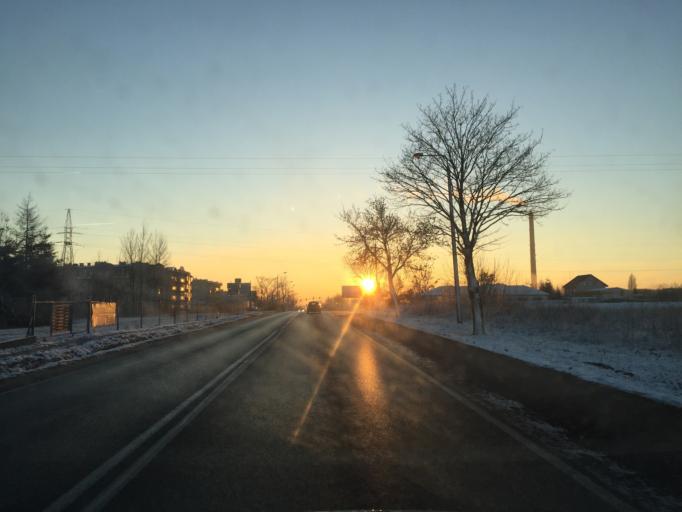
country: PL
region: Kujawsko-Pomorskie
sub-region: Powiat torunski
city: Lubicz Dolny
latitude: 53.0539
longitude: 18.7113
